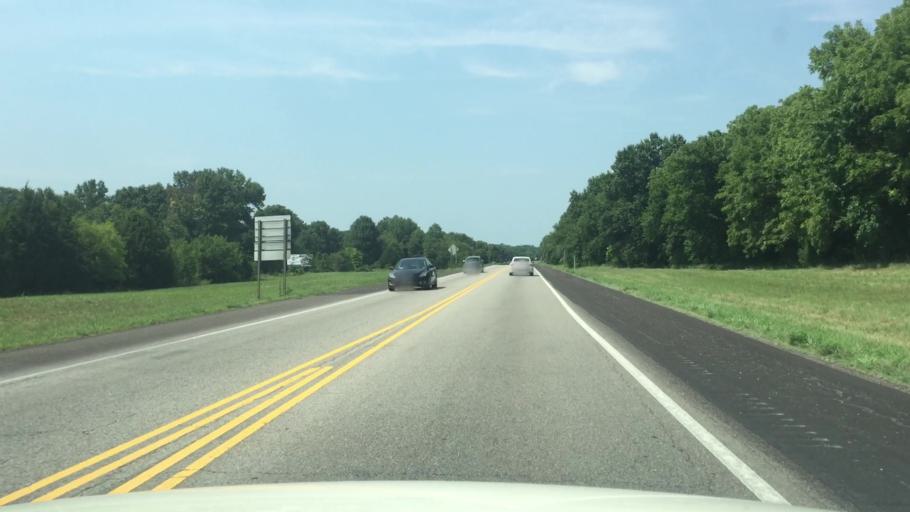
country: US
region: Kansas
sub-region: Crawford County
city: Pittsburg
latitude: 37.3989
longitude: -94.7203
